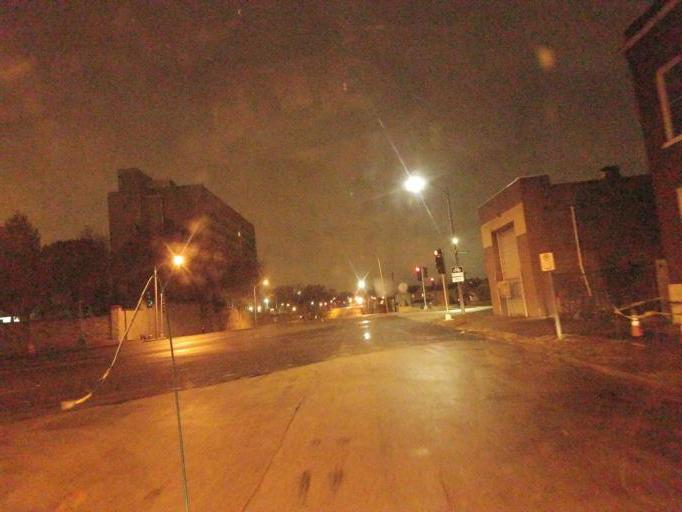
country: US
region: Missouri
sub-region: City of Saint Louis
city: St. Louis
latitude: 38.6562
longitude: -90.2029
